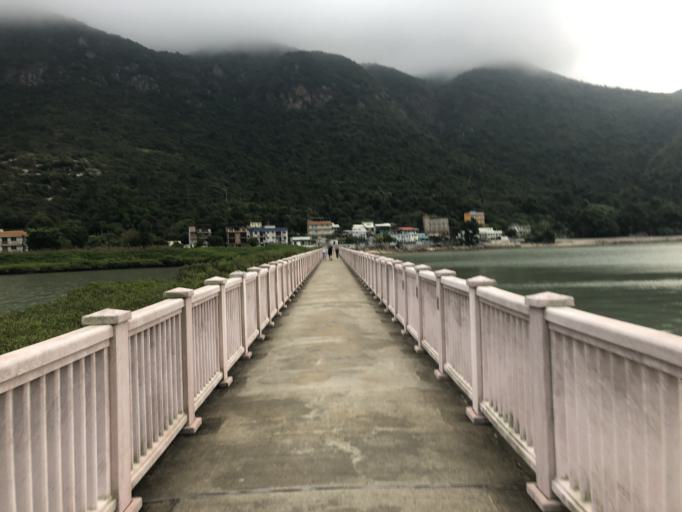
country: HK
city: Tai O
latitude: 22.2488
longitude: 113.8611
